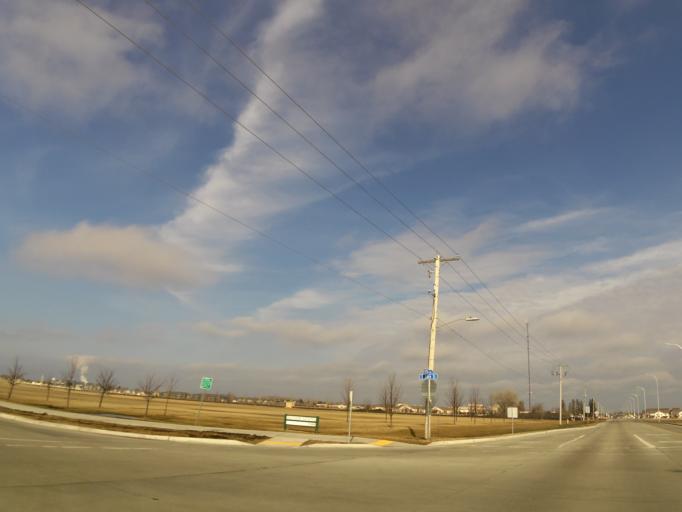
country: US
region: North Dakota
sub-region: Grand Forks County
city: Grand Forks
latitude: 47.8749
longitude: -97.0577
